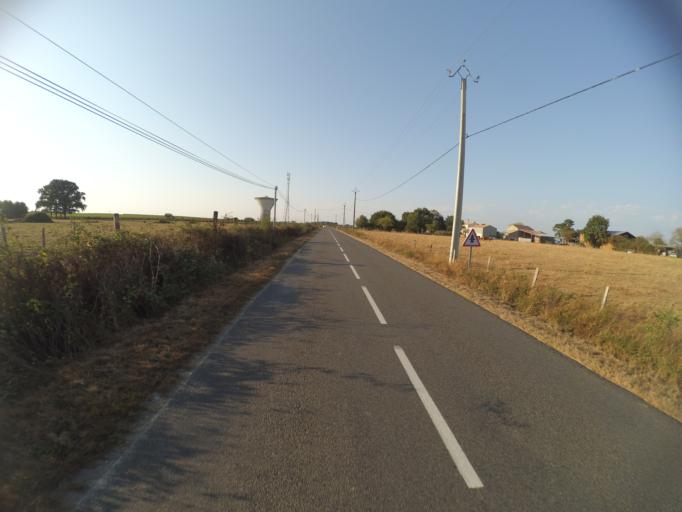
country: FR
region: Pays de la Loire
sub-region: Departement de la Loire-Atlantique
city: La Planche
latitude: 47.0432
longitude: -1.4151
